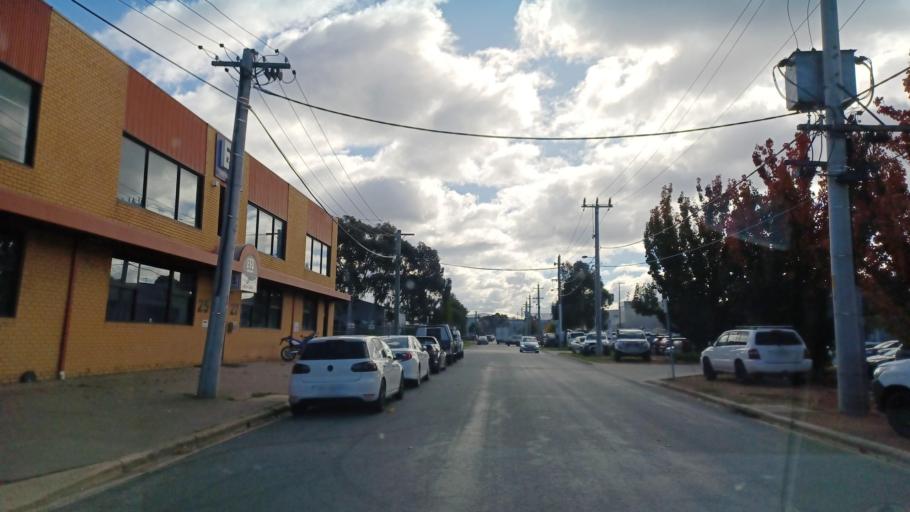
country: AU
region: Australian Capital Territory
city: Kaleen
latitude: -35.2193
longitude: 149.1437
